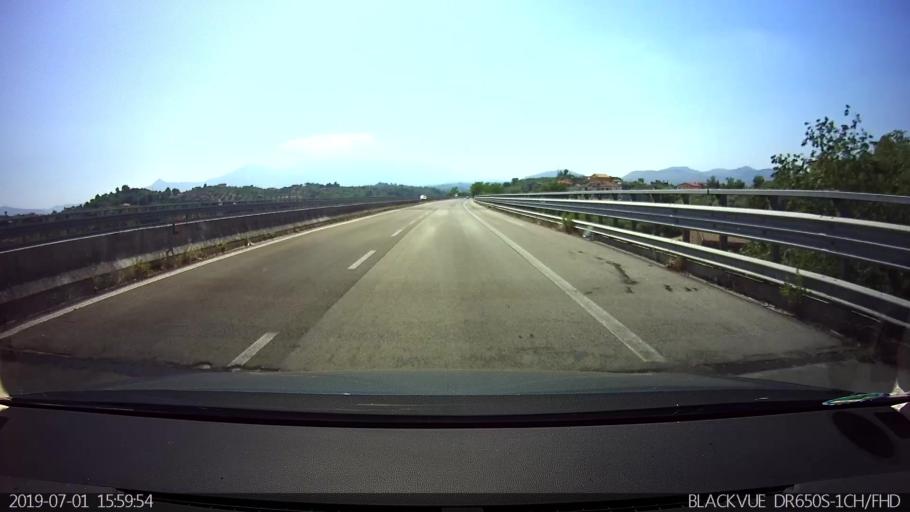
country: IT
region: Latium
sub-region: Provincia di Frosinone
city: Sant'Angelo in Villa-Giglio
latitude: 41.6614
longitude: 13.4101
